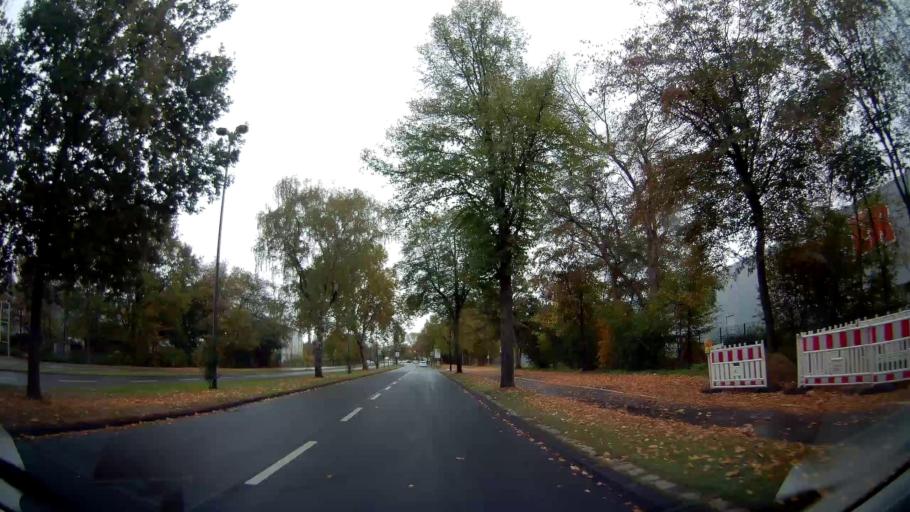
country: DE
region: North Rhine-Westphalia
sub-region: Regierungsbezirk Munster
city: Gelsenkirchen
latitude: 51.5493
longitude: 7.0798
